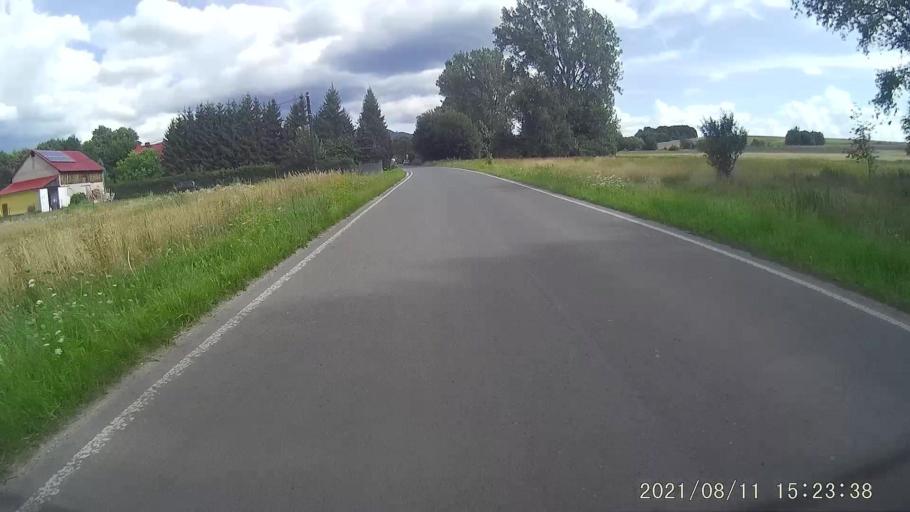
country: PL
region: Lower Silesian Voivodeship
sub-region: Powiat klodzki
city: Bystrzyca Klodzka
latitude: 50.2723
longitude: 16.6919
